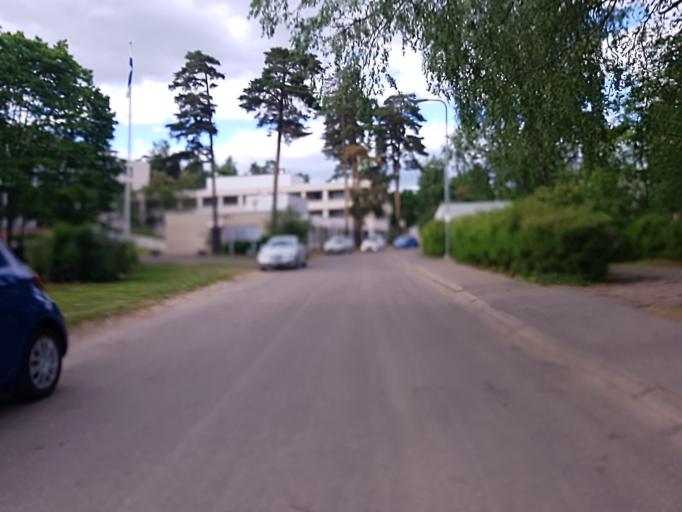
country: FI
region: Uusimaa
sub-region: Helsinki
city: Teekkarikylae
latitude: 60.2267
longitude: 24.8464
